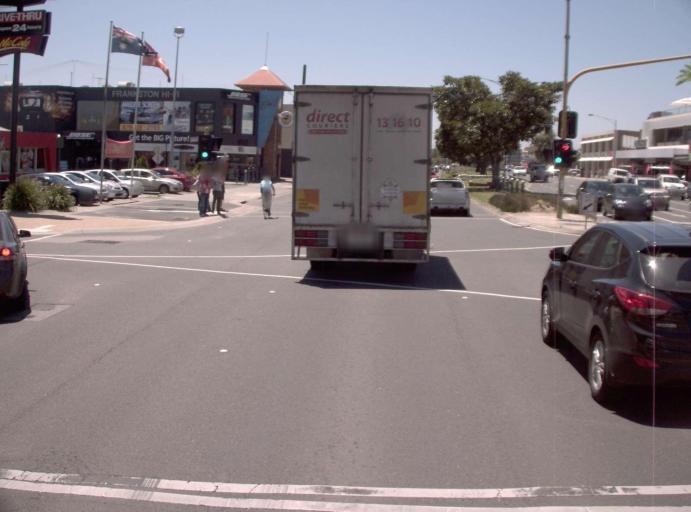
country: AU
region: Victoria
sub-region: Frankston
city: Frankston
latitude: -38.1431
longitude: 145.1210
